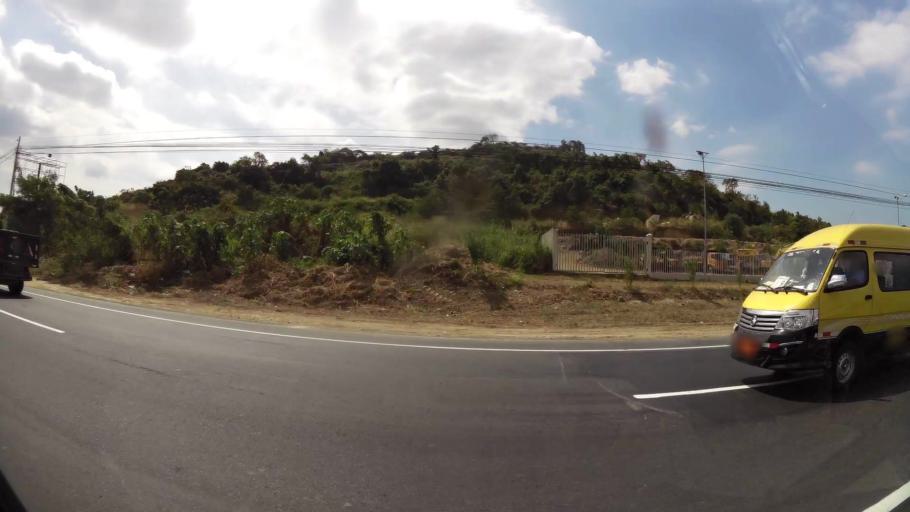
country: EC
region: Guayas
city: El Triunfo
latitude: -2.0589
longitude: -79.9233
